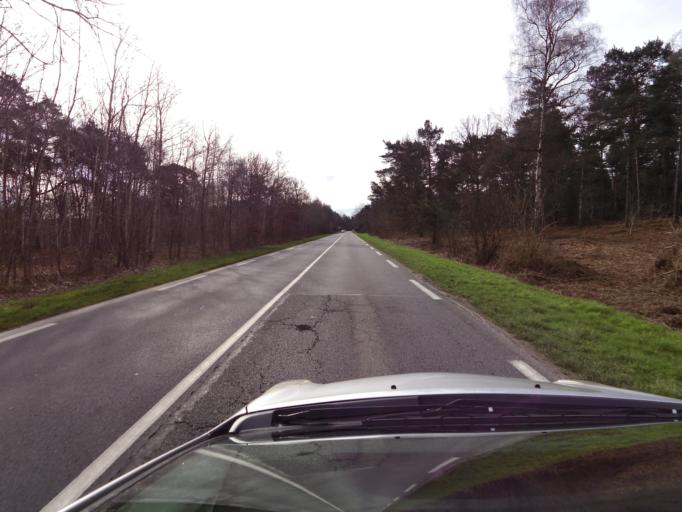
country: FR
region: Picardie
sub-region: Departement de l'Oise
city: Ver-sur-Launette
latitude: 49.1412
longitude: 2.6843
